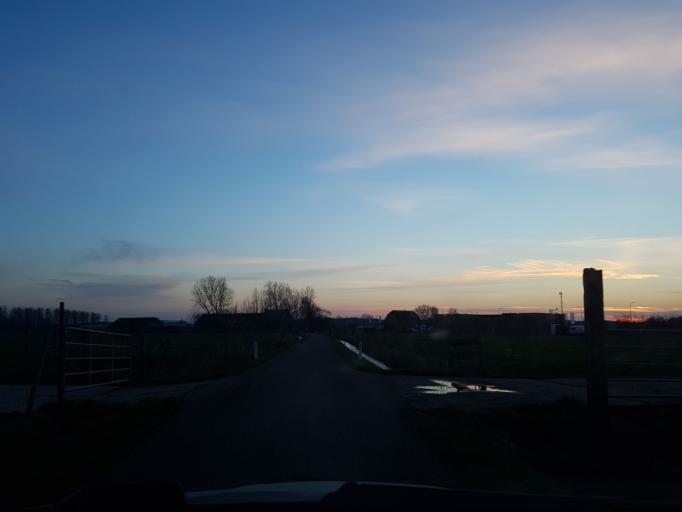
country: NL
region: South Holland
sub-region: Gemeente Noordwijk
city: Noordwijk-Binnen
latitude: 52.2175
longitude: 4.4407
